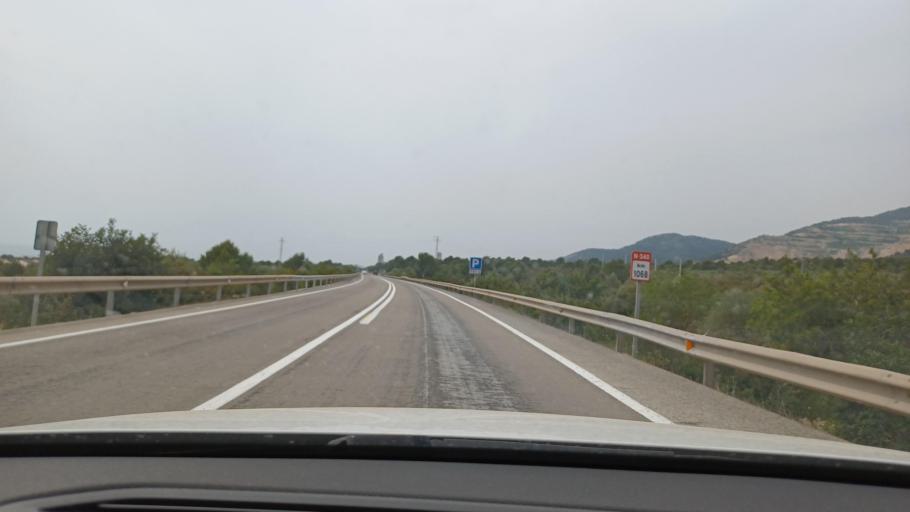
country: ES
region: Catalonia
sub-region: Provincia de Tarragona
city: Sant Carles de la Rapita
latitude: 40.5973
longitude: 0.5579
